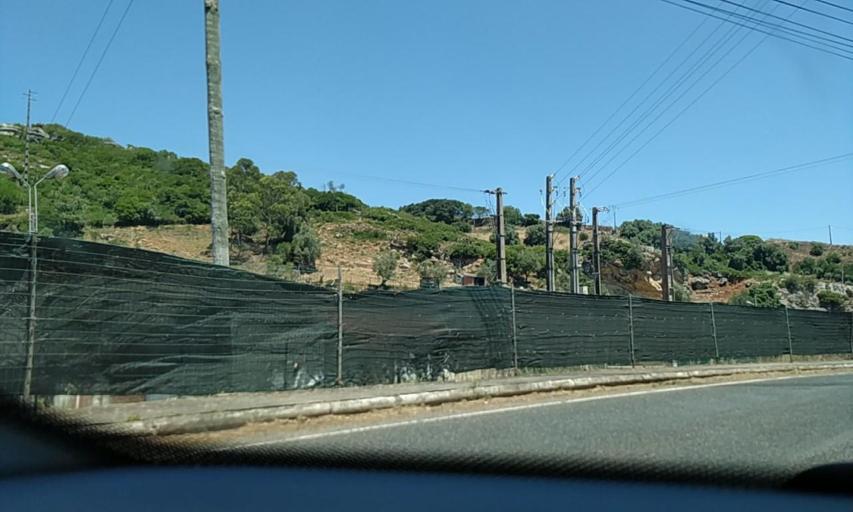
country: PT
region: Lisbon
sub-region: Odivelas
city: Canecas
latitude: 38.8653
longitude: -9.2120
